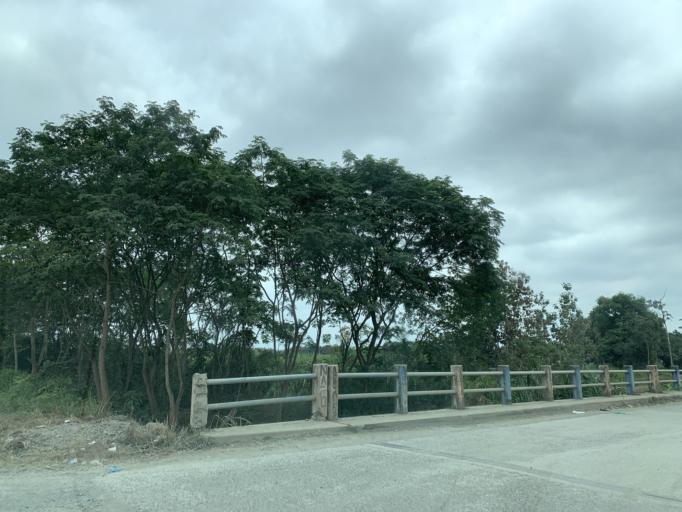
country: EC
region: Guayas
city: Coronel Marcelino Mariduena
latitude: -2.3197
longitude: -79.4710
